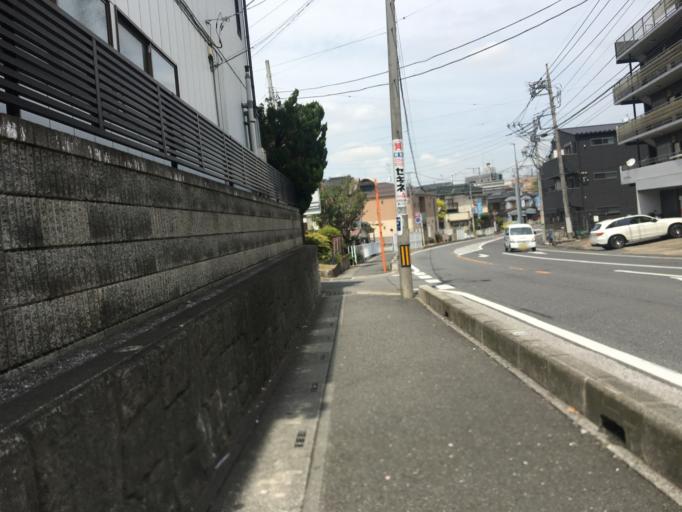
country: JP
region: Saitama
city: Oi
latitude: 35.8463
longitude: 139.5428
